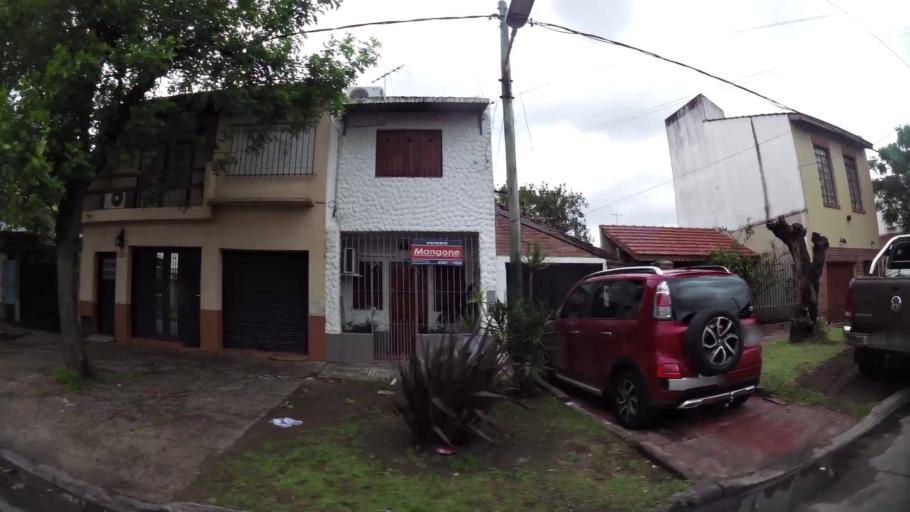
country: AR
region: Buenos Aires
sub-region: Partido de Lomas de Zamora
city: Lomas de Zamora
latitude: -34.7523
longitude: -58.3701
